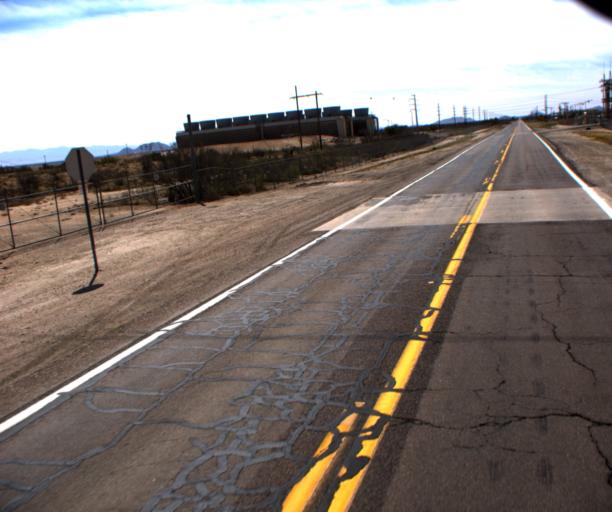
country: US
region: Arizona
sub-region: Cochise County
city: Willcox
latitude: 32.0646
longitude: -109.8934
